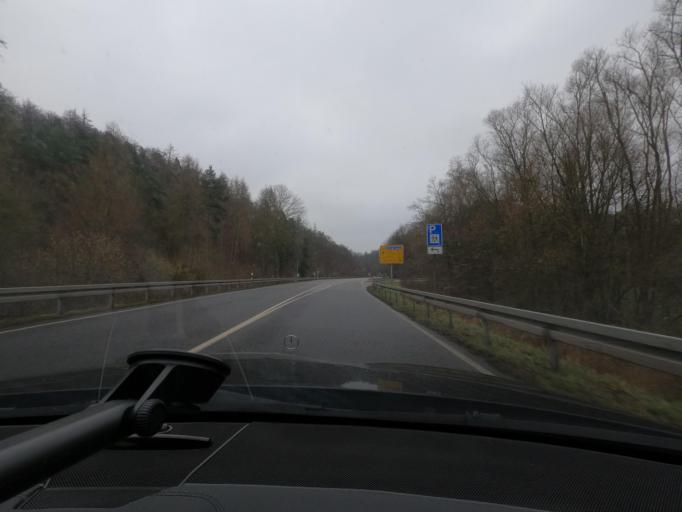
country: DE
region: Hesse
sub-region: Regierungsbezirk Kassel
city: Bad Arolsen
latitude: 51.3606
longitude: 9.0586
